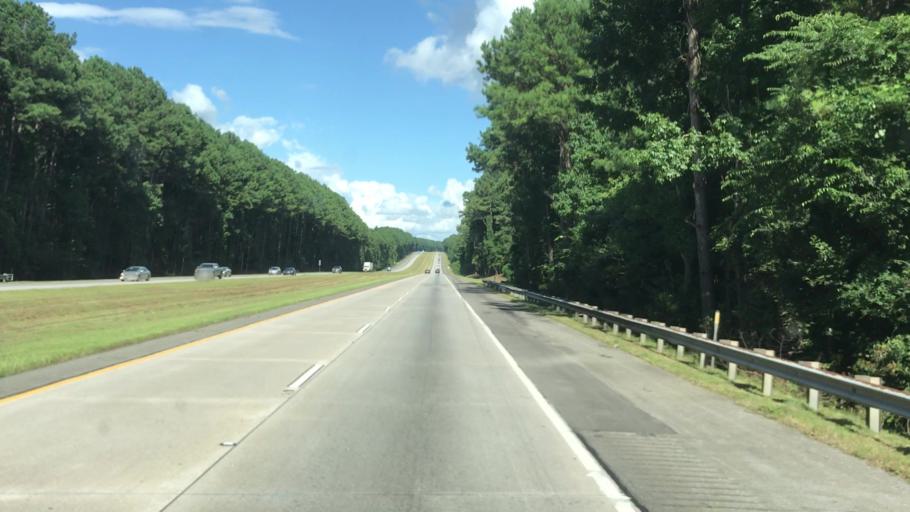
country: US
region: Georgia
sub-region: Greene County
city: Greensboro
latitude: 33.5484
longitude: -83.1532
